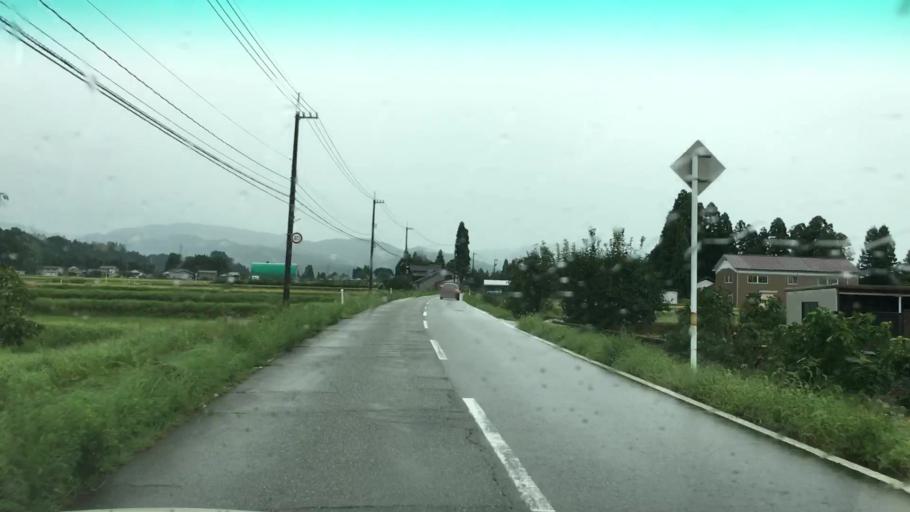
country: JP
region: Toyama
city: Kamiichi
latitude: 36.6221
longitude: 137.3233
